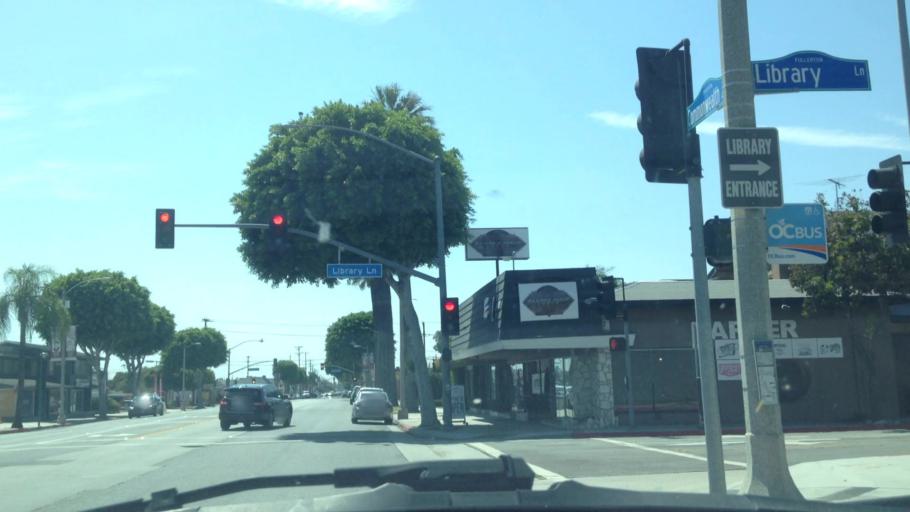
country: US
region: California
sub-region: Orange County
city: Fullerton
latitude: 33.8704
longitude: -117.9312
